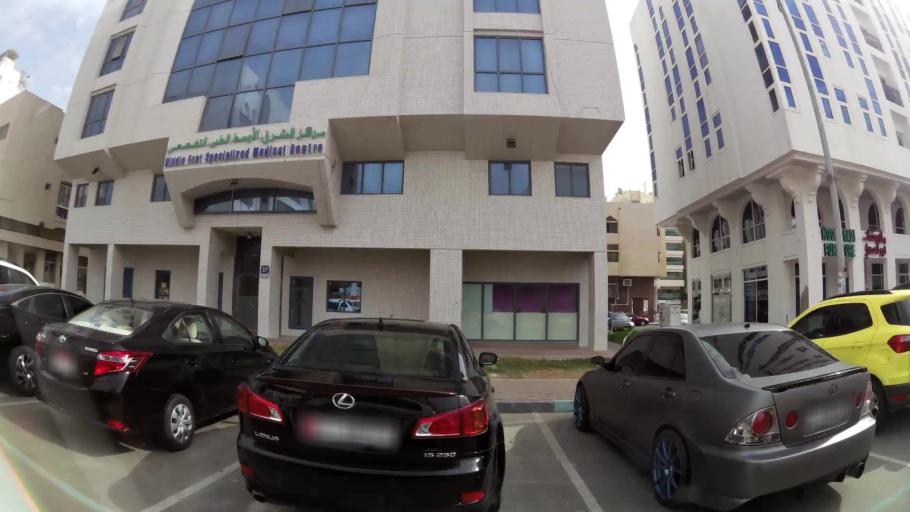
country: AE
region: Abu Dhabi
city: Abu Dhabi
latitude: 24.4629
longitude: 54.3835
